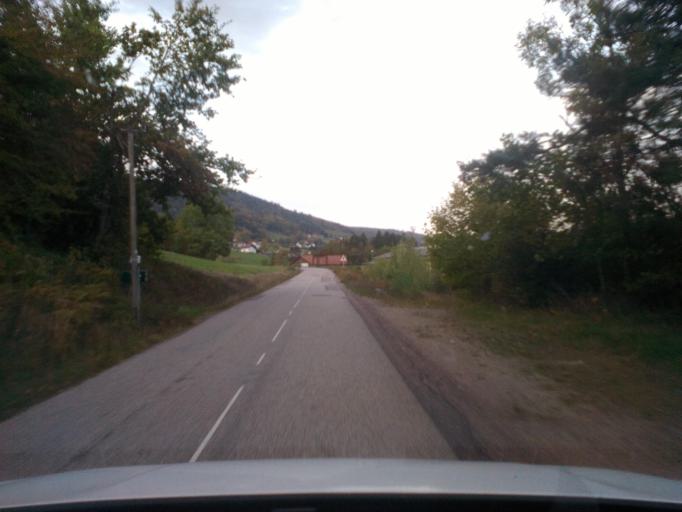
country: FR
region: Lorraine
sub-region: Departement des Vosges
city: Le Syndicat
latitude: 48.0517
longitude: 6.6855
